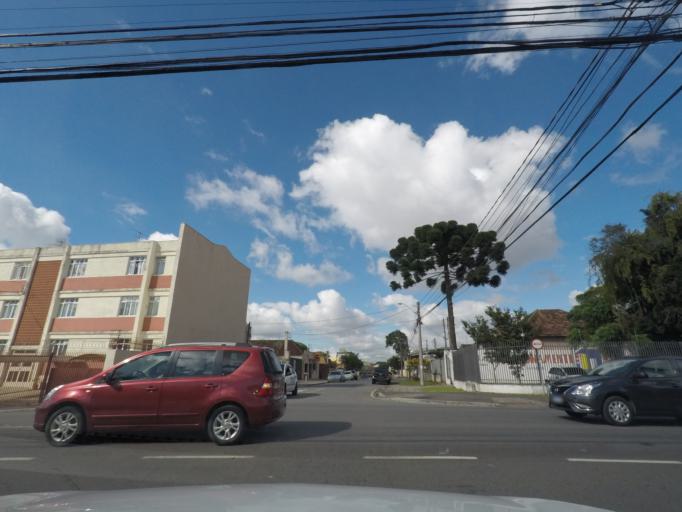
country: BR
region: Parana
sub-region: Curitiba
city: Curitiba
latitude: -25.4486
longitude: -49.2567
